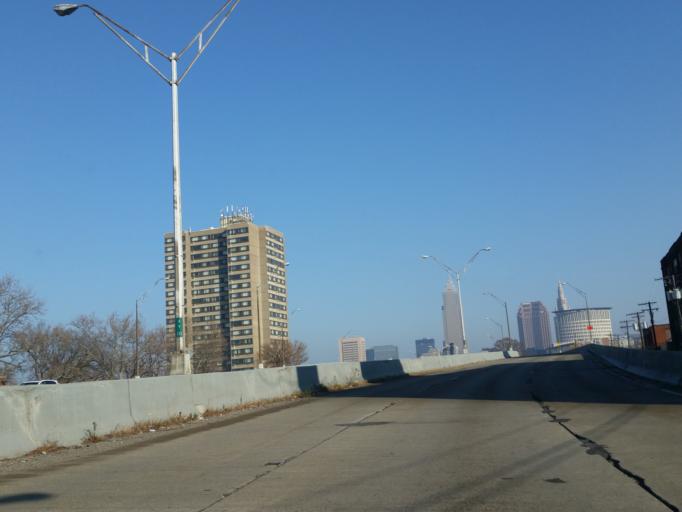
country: US
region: Ohio
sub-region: Cuyahoga County
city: Cleveland
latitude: 41.4905
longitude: -81.7115
